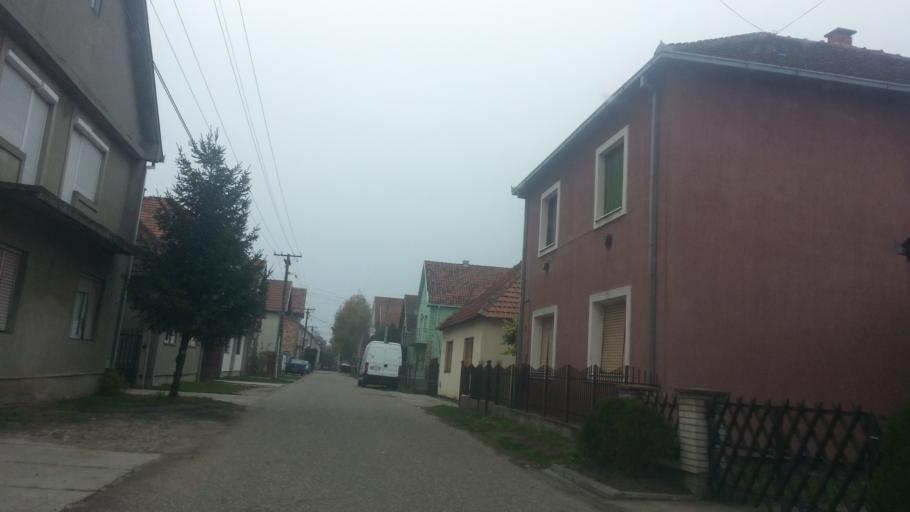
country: RS
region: Autonomna Pokrajina Vojvodina
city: Nova Pazova
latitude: 44.9528
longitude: 20.2151
